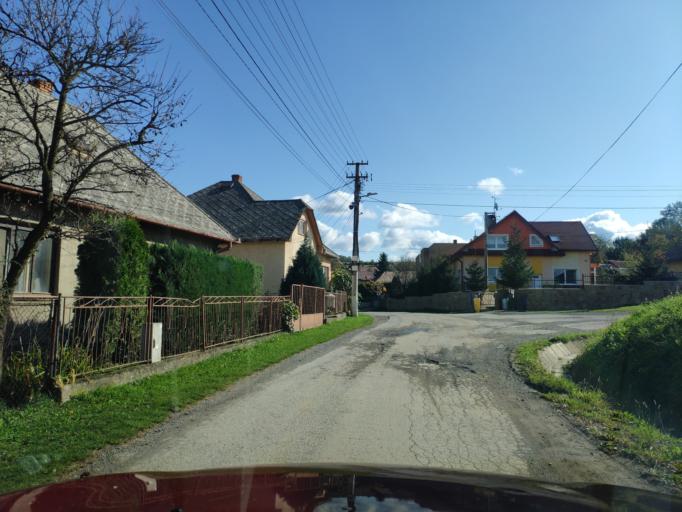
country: SK
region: Presovsky
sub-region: Okres Presov
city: Presov
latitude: 48.9423
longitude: 21.2859
